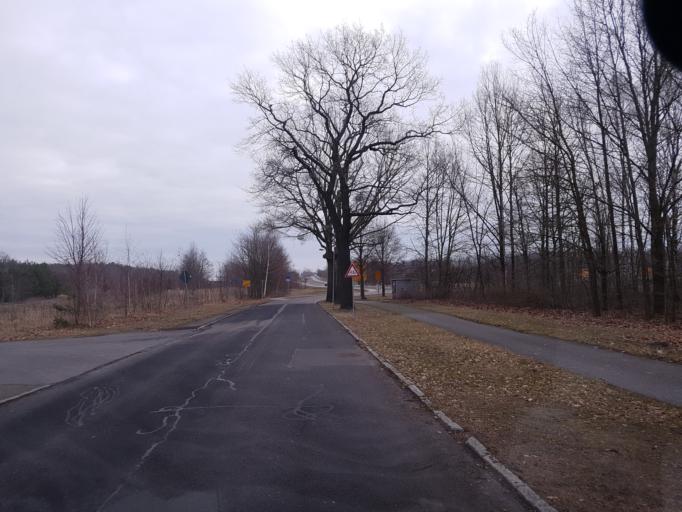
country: DE
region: Brandenburg
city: Senftenberg
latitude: 51.5271
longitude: 13.9612
